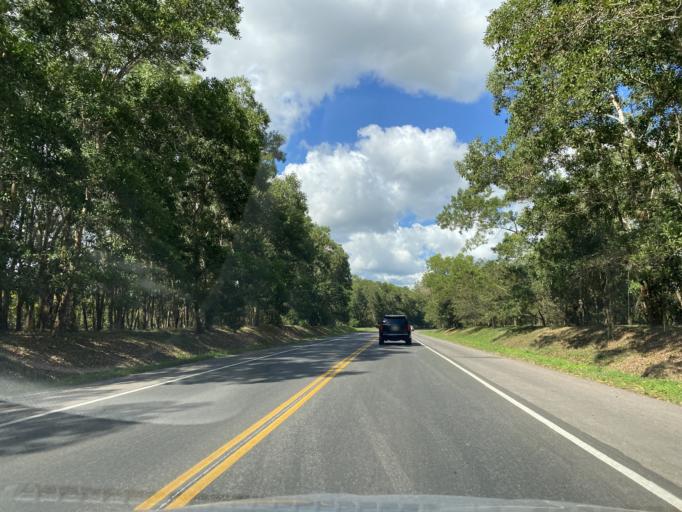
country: DO
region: Monte Plata
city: Monte Plata
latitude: 18.7479
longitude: -69.7657
